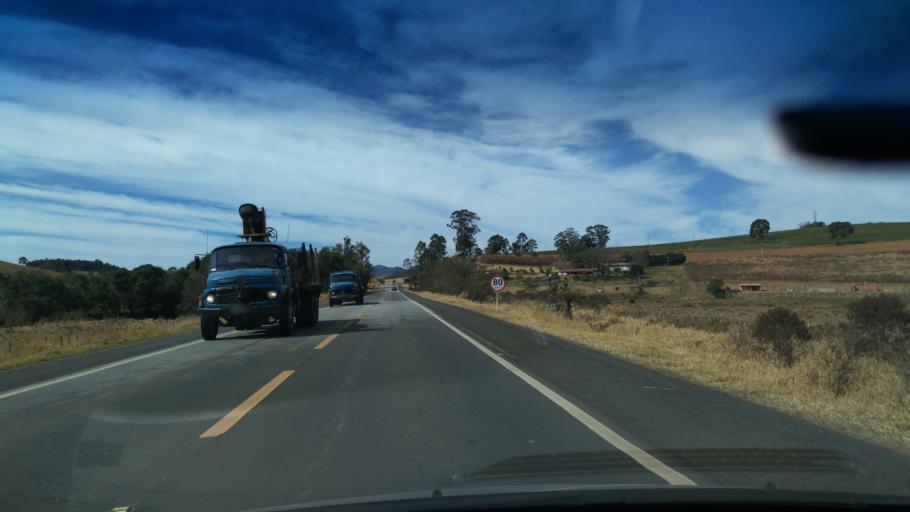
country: BR
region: Minas Gerais
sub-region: Borda Da Mata
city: Borda da Mata
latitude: -22.0579
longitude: -46.2846
